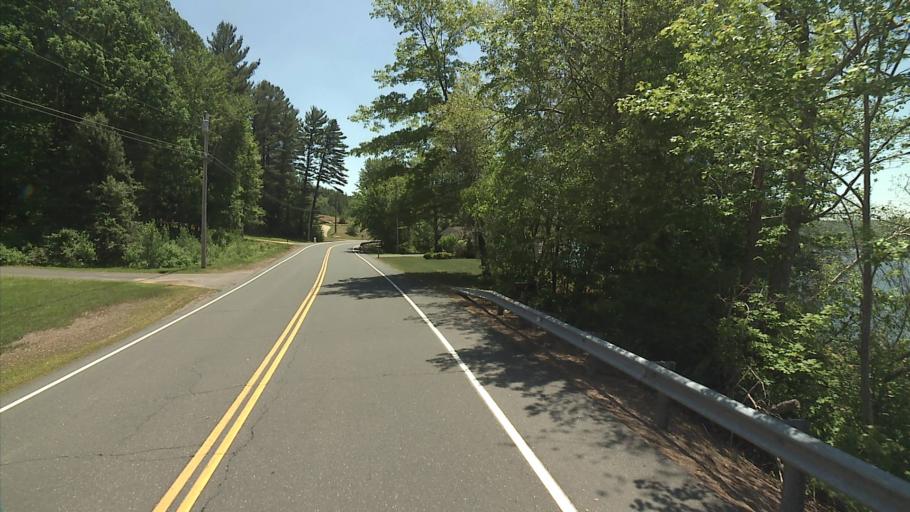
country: US
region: Connecticut
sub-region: Tolland County
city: Stafford
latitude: 42.0013
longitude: -72.2554
